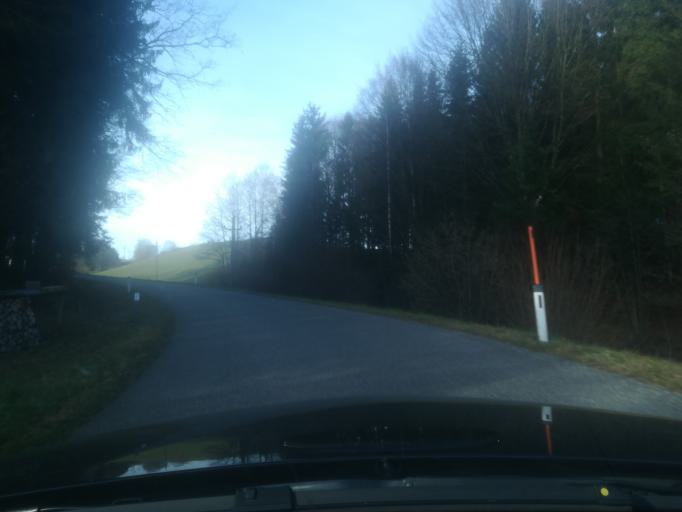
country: AT
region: Upper Austria
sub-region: Politischer Bezirk Perg
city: Perg
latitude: 48.3231
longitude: 14.6595
